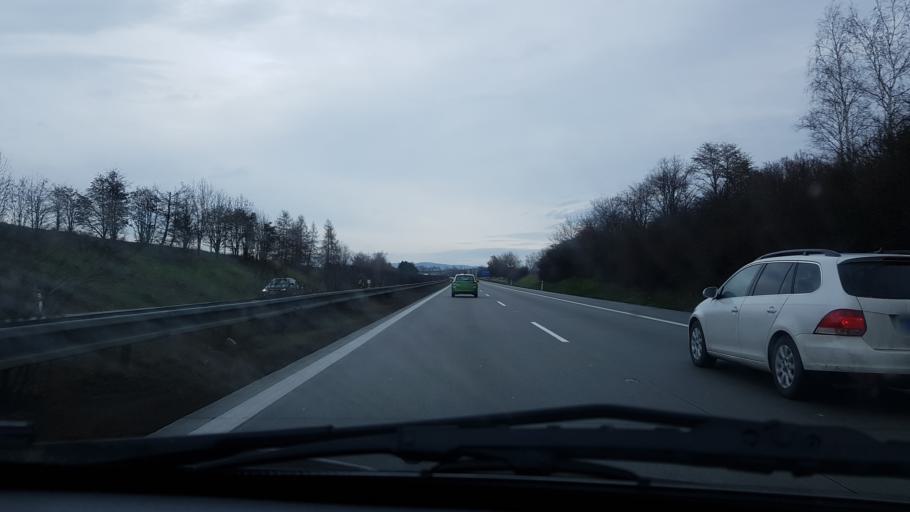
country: CZ
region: Olomoucky
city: Doloplazy
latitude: 49.5850
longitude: 17.4265
